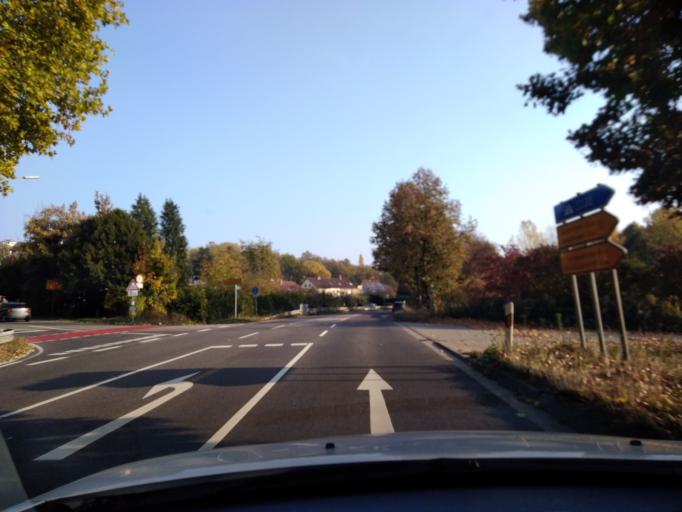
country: DE
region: Saarland
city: Kleinblittersdorf
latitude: 49.1481
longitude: 7.0438
